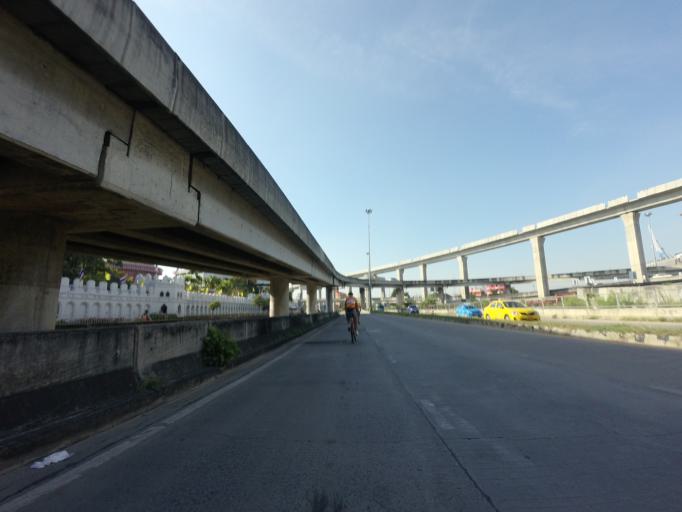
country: TH
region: Samut Prakan
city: Samut Prakan
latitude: 13.6295
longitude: 100.5887
